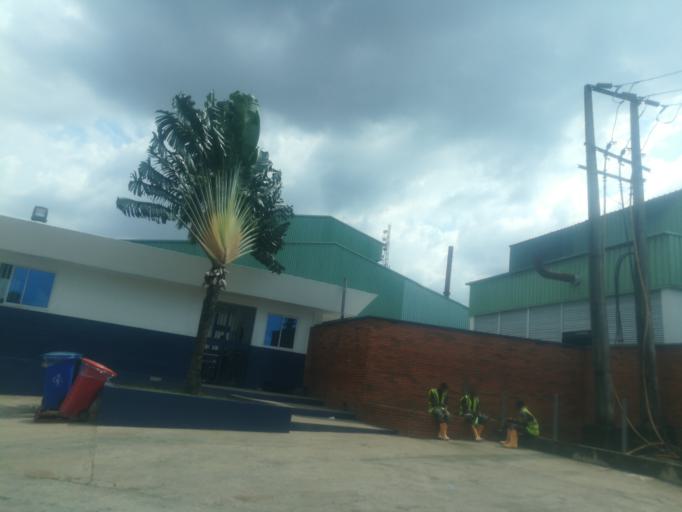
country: NG
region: Oyo
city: Ibadan
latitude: 7.4105
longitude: 3.8686
